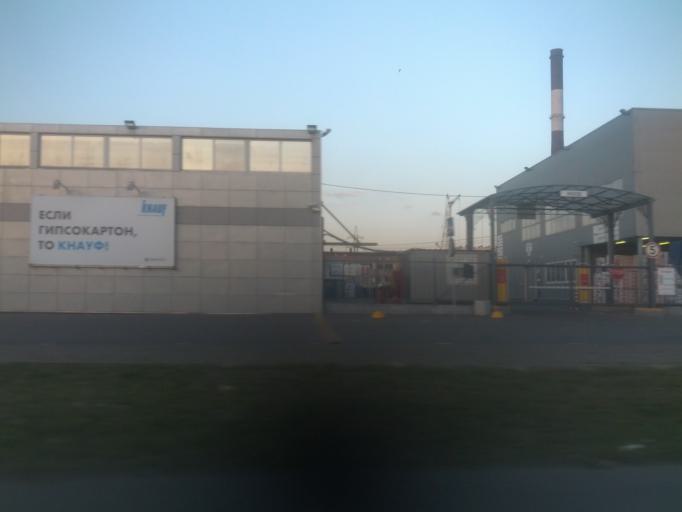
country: RU
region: St.-Petersburg
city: Staraya Derevnya
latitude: 59.9968
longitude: 30.2339
